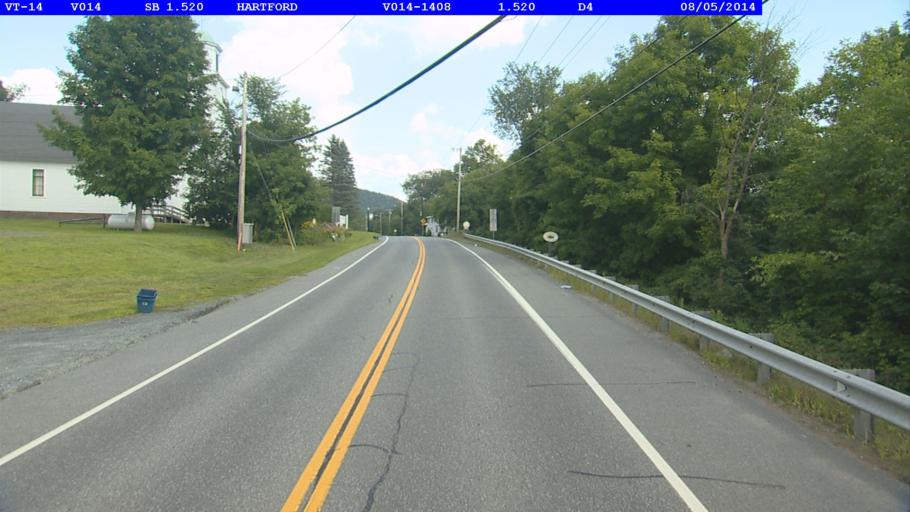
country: US
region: Vermont
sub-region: Windsor County
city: White River Junction
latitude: 43.6616
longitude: -72.3460
